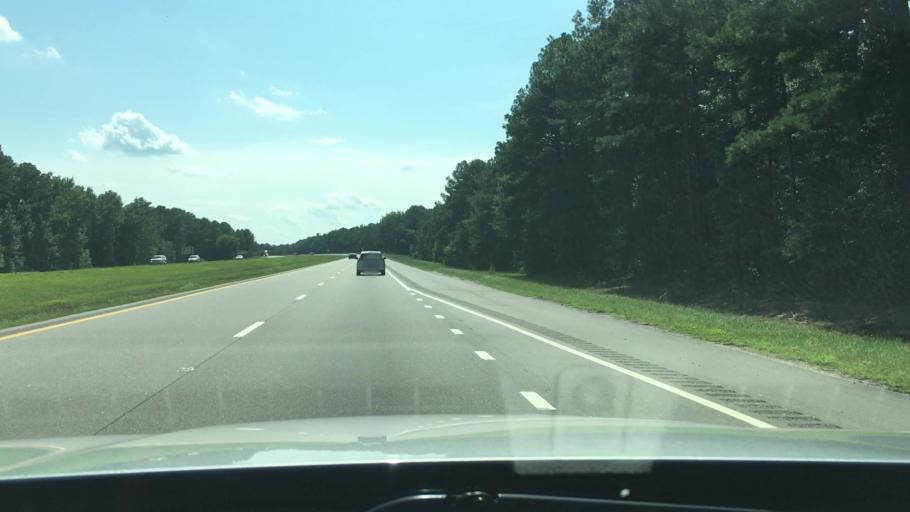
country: US
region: North Carolina
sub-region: Cumberland County
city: Hope Mills
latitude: 34.9355
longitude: -78.9302
